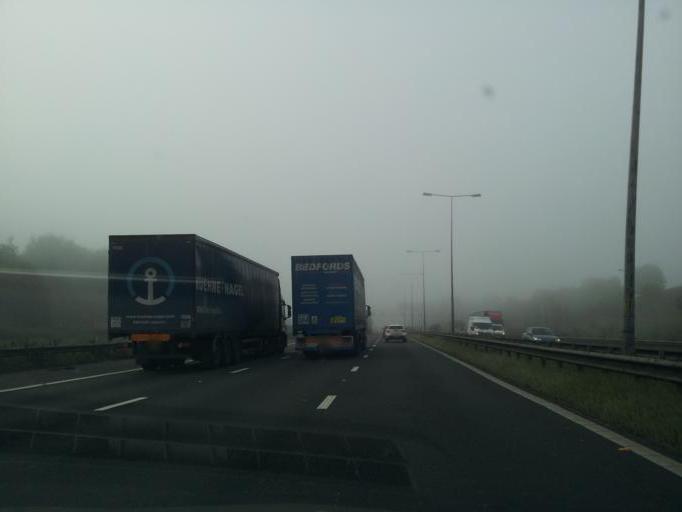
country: GB
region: England
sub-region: Kirklees
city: Cleckheaton
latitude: 53.7328
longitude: -1.7296
